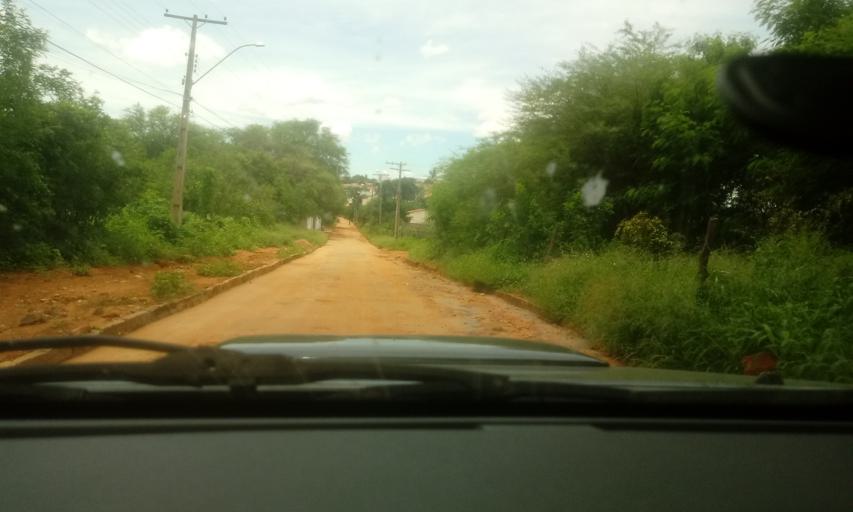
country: BR
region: Bahia
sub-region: Riacho De Santana
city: Riacho de Santana
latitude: -13.6054
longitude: -42.9461
